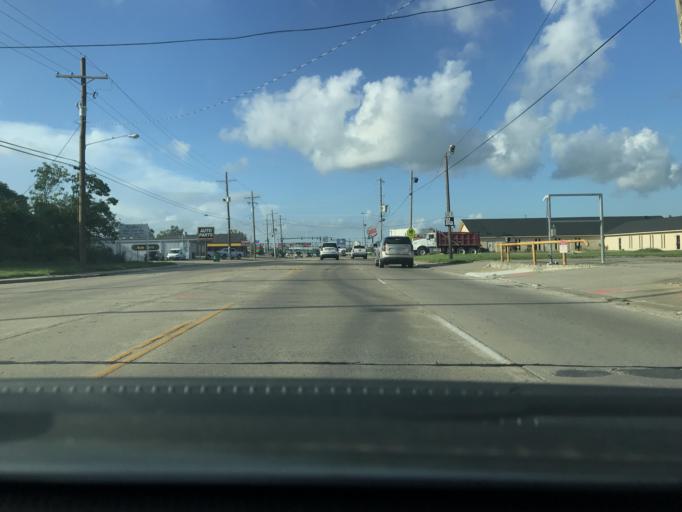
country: US
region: Louisiana
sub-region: Calcasieu Parish
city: Westlake
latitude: 30.2443
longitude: -93.2582
